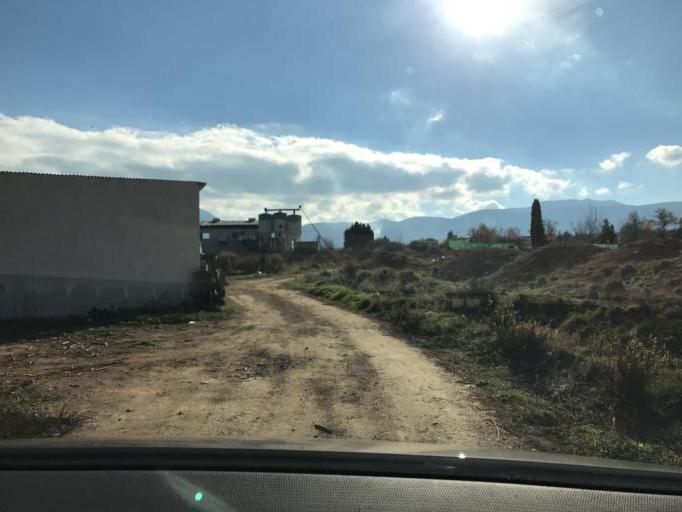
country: ES
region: Andalusia
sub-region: Provincia de Granada
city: Gojar
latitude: 37.1000
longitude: -3.6183
